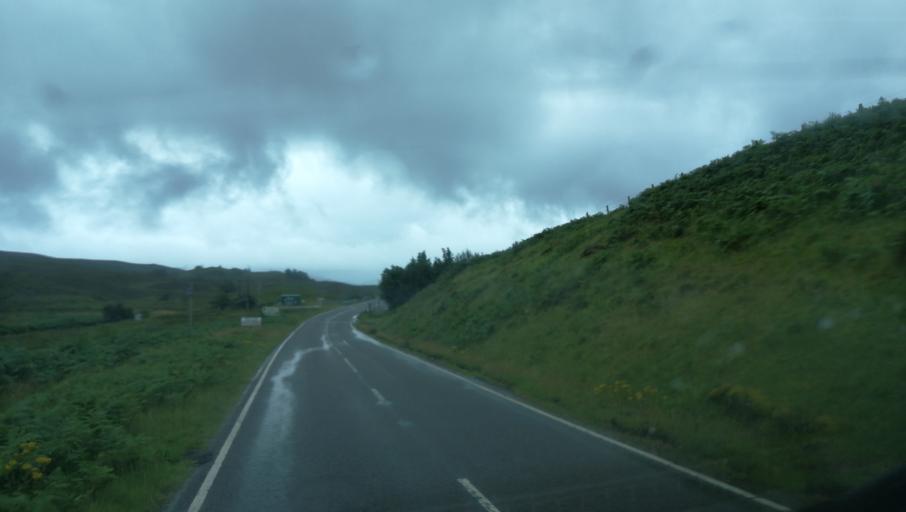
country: GB
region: Scotland
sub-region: Highland
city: Ullapool
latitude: 58.0004
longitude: -5.1025
